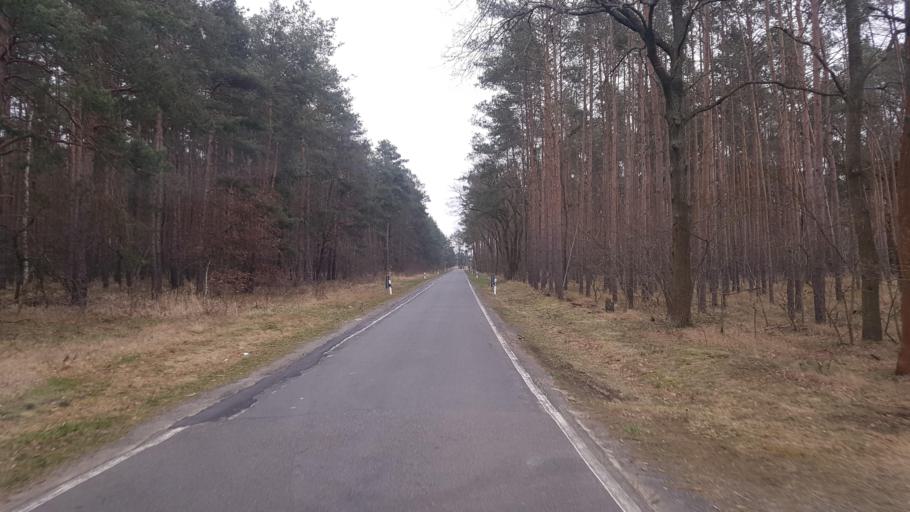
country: DE
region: Brandenburg
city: Herzberg
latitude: 51.6864
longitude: 13.1976
